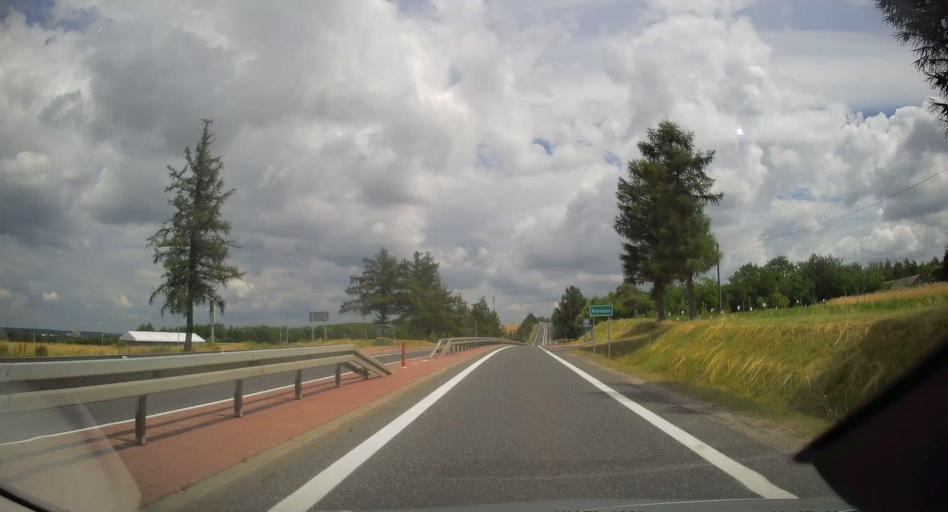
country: PL
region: Subcarpathian Voivodeship
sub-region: Powiat ropczycko-sedziszowski
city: Ropczyce
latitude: 50.0617
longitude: 21.5682
